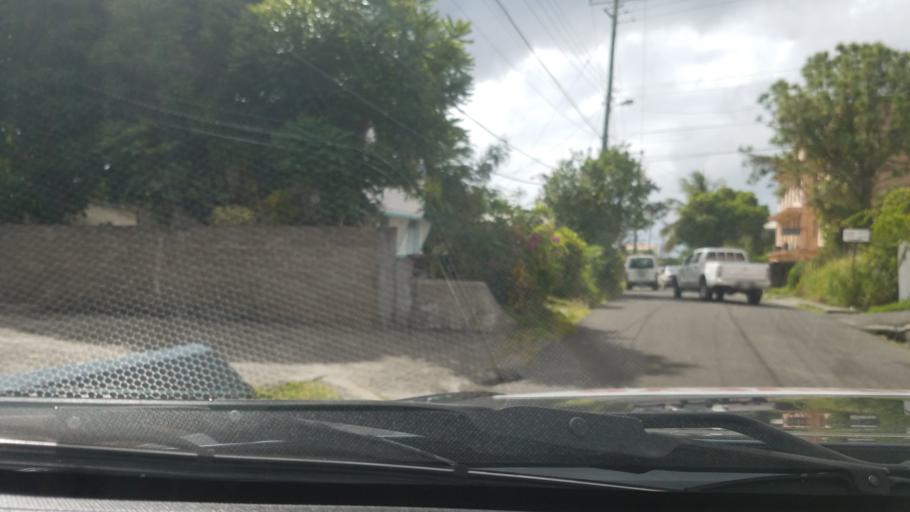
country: LC
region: Castries Quarter
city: Bisee
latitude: 14.0180
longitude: -60.9886
